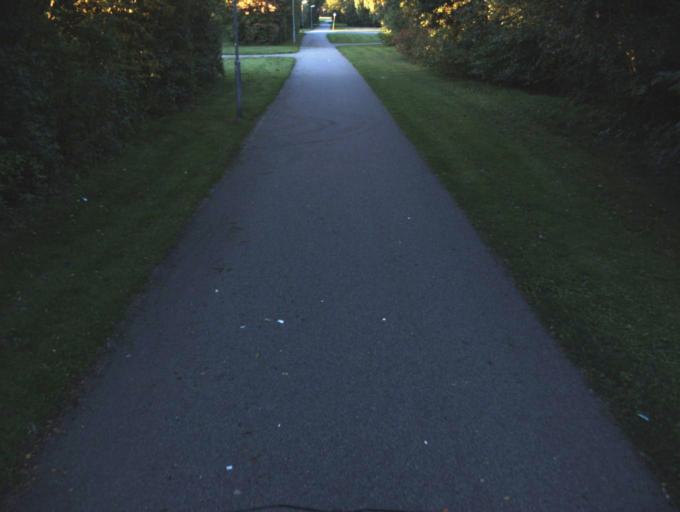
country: SE
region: Skane
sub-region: Helsingborg
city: Barslov
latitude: 56.0093
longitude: 12.7988
